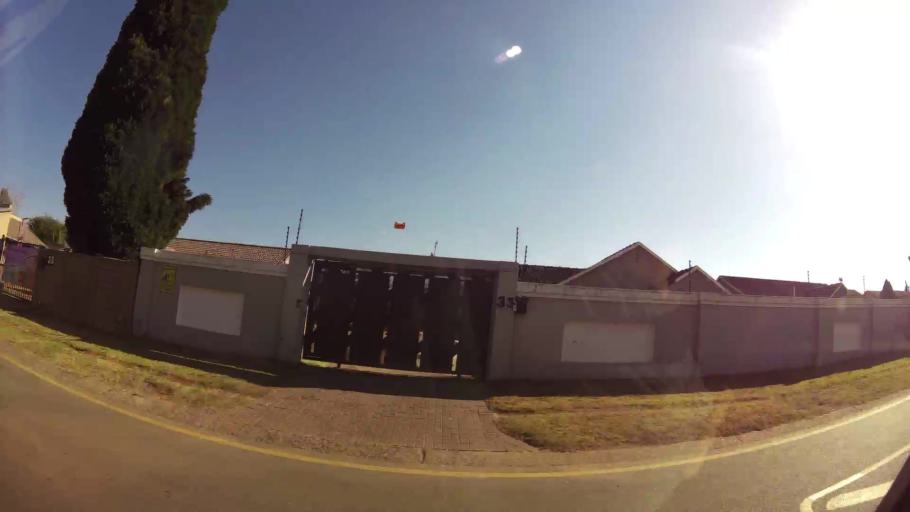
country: ZA
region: Gauteng
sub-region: Ekurhuleni Metropolitan Municipality
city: Germiston
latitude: -26.3371
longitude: 28.0978
